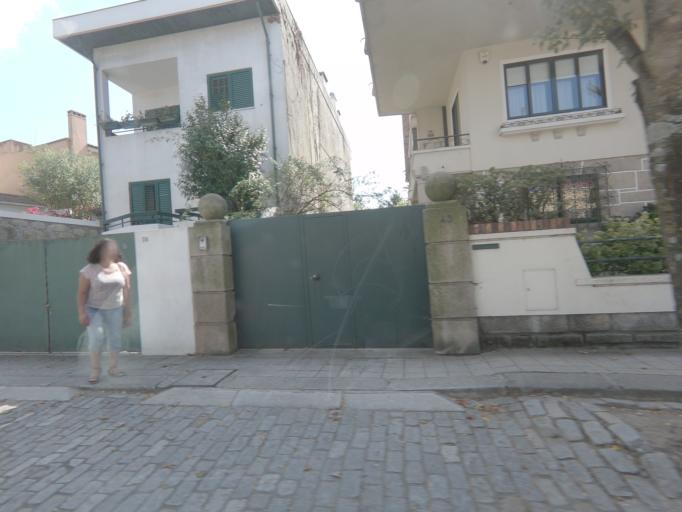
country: PT
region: Porto
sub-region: Porto
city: Porto
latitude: 41.1635
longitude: -8.6281
